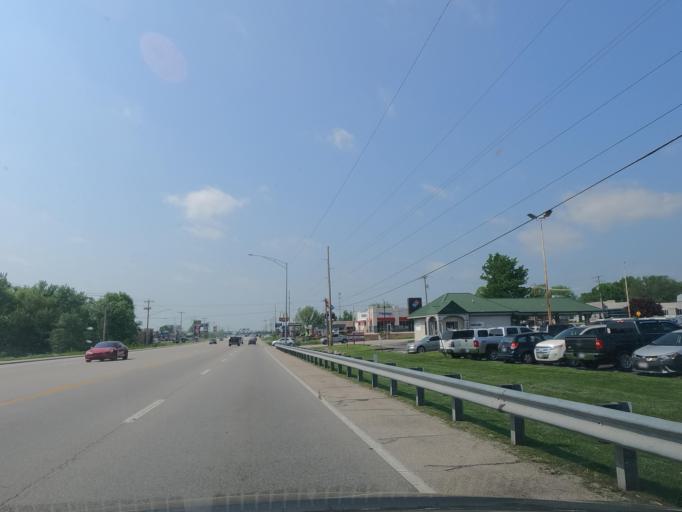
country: US
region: Missouri
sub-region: Greene County
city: Springfield
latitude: 37.1425
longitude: -93.2962
